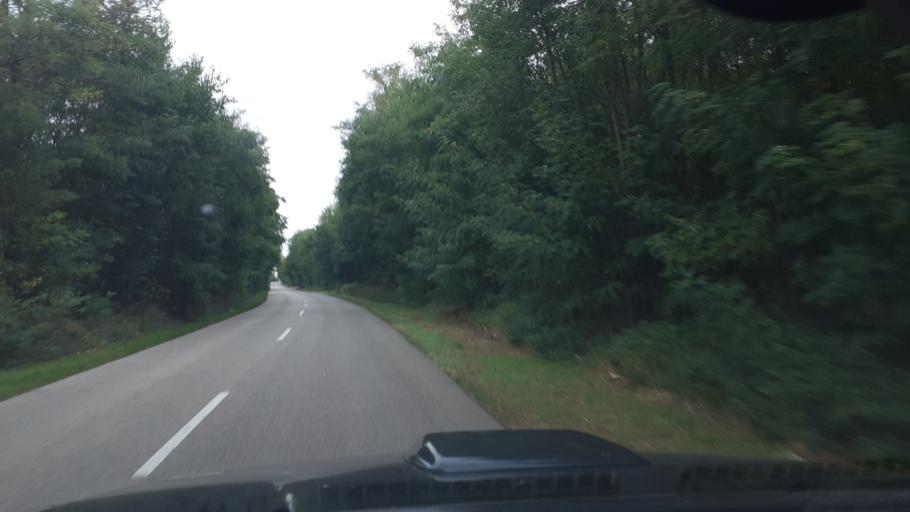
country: HU
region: Fejer
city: Baracs
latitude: 46.8442
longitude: 18.8904
